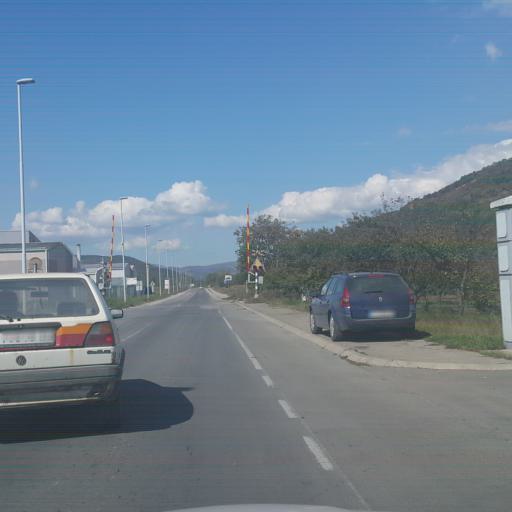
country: RS
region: Central Serbia
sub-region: Pirotski Okrug
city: Pirot
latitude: 43.1789
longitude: 22.5773
